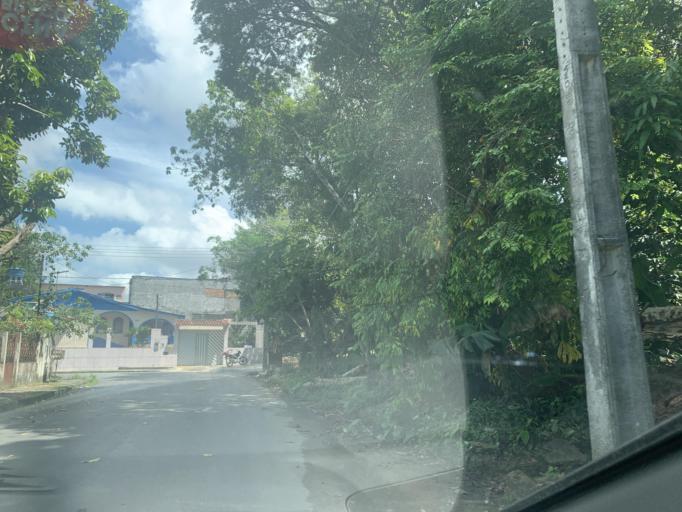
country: BR
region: Amazonas
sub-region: Manaus
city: Manaus
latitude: -3.1010
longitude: -59.9643
